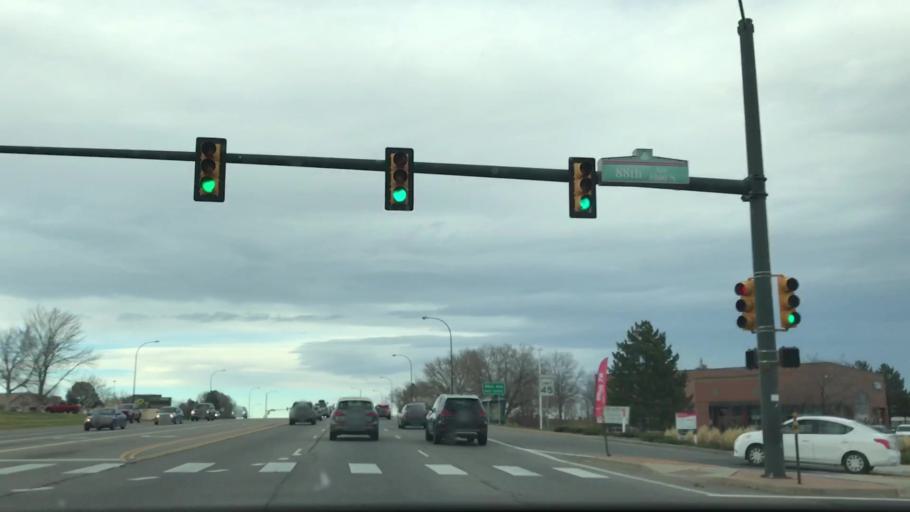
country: US
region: Colorado
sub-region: Adams County
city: Westminster
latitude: 39.8565
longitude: -105.0816
